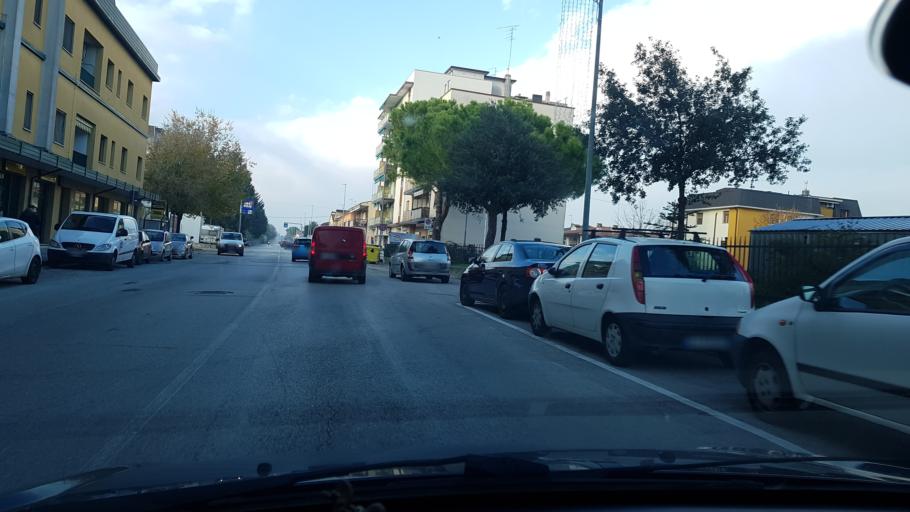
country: IT
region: Friuli Venezia Giulia
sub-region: Provincia di Gorizia
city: Ronchi dei Legionari
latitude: 45.8294
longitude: 13.5012
